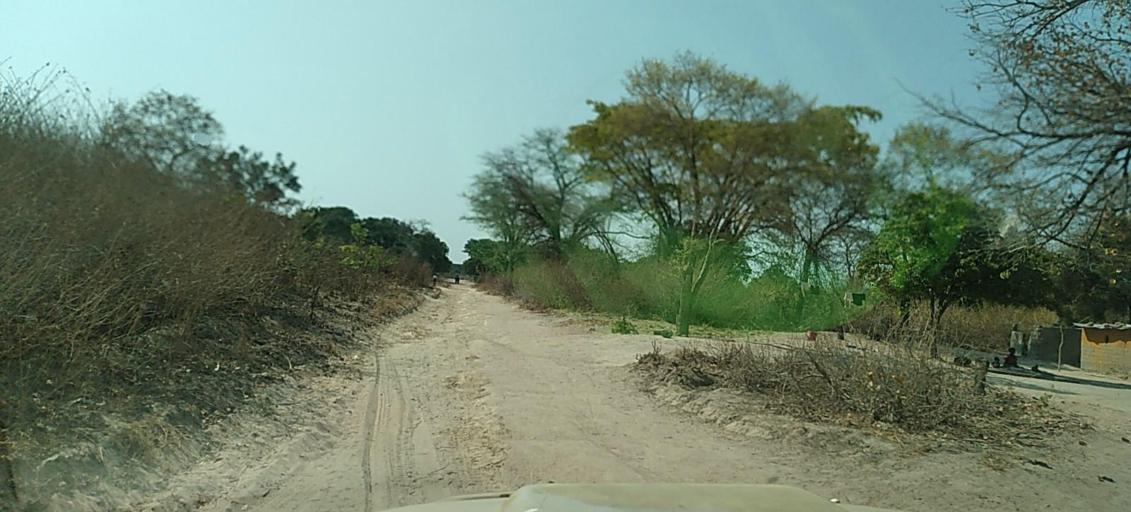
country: ZM
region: North-Western
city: Kalengwa
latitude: -13.3566
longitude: 24.8616
